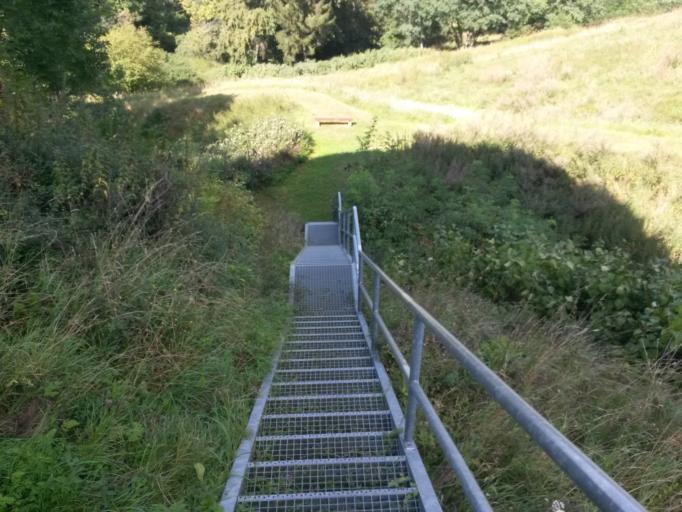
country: DE
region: Brandenburg
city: Schoneberg
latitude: 52.9807
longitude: 14.1156
